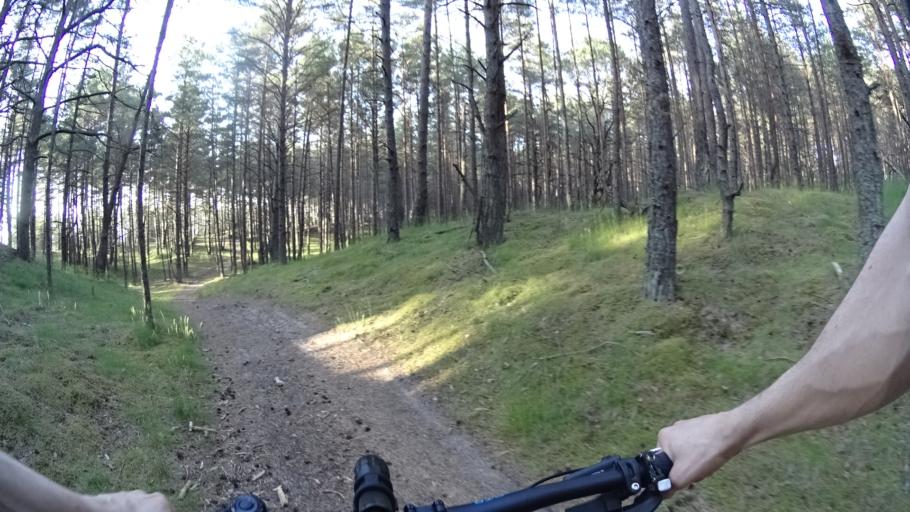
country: LV
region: Riga
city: Jaunciems
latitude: 57.1092
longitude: 24.1832
